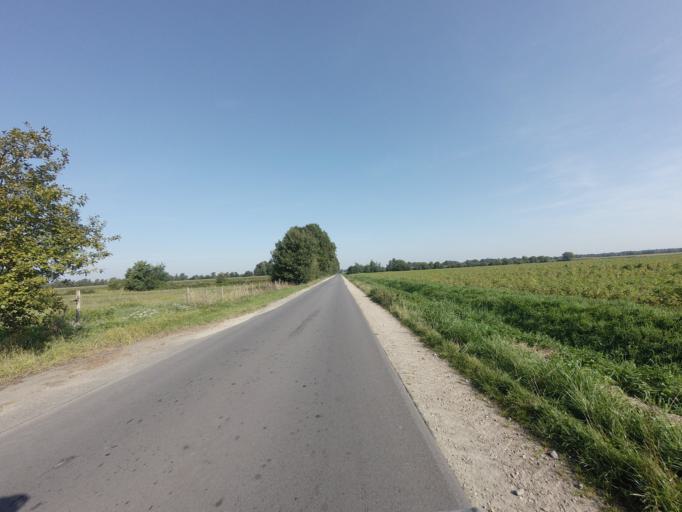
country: DE
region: Lower Saxony
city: Laar
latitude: 52.5823
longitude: 6.7799
